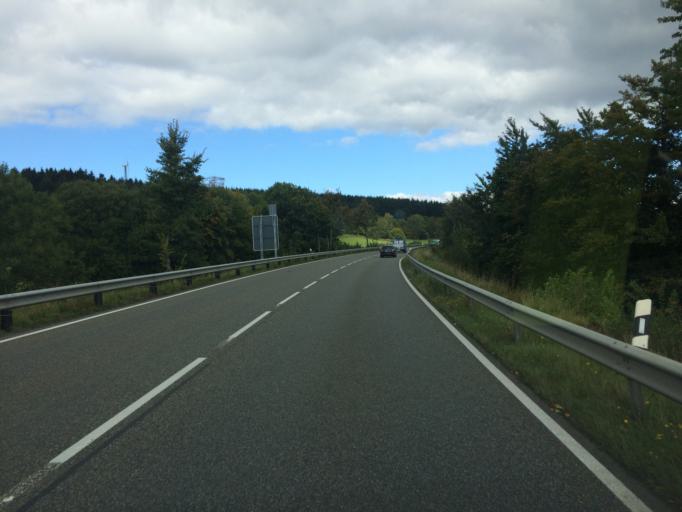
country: DE
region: Rheinland-Pfalz
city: Salzburg
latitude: 50.6654
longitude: 8.0570
